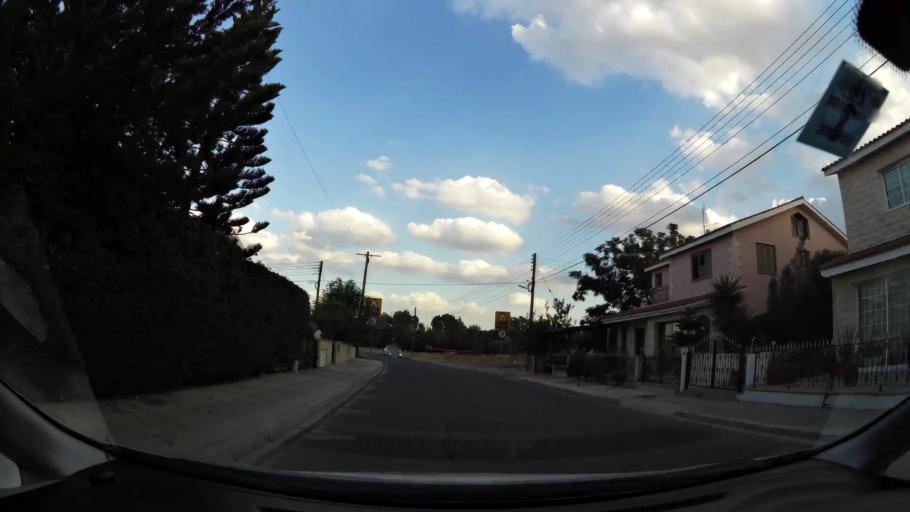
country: CY
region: Lefkosia
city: Kato Deftera
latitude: 35.1236
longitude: 33.3102
